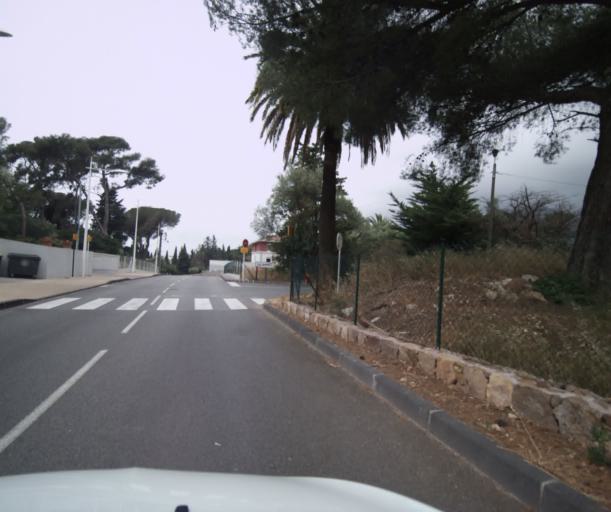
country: FR
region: Provence-Alpes-Cote d'Azur
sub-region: Departement du Var
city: La Valette-du-Var
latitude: 43.1227
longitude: 5.9855
